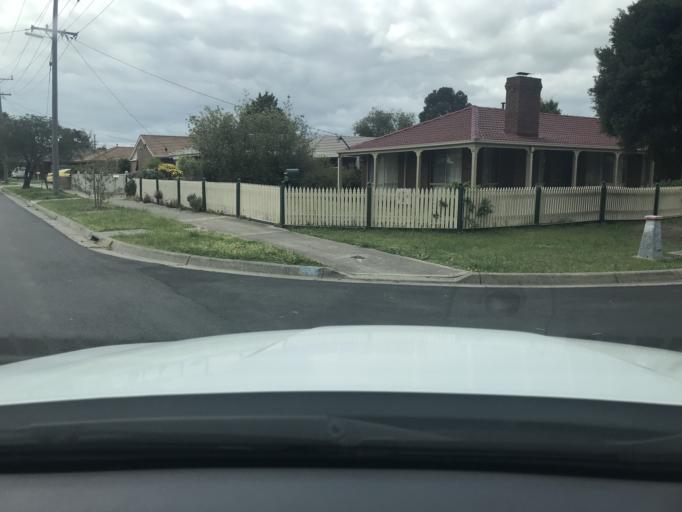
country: AU
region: Victoria
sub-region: Hume
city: Craigieburn
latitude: -37.5917
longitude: 144.9250
